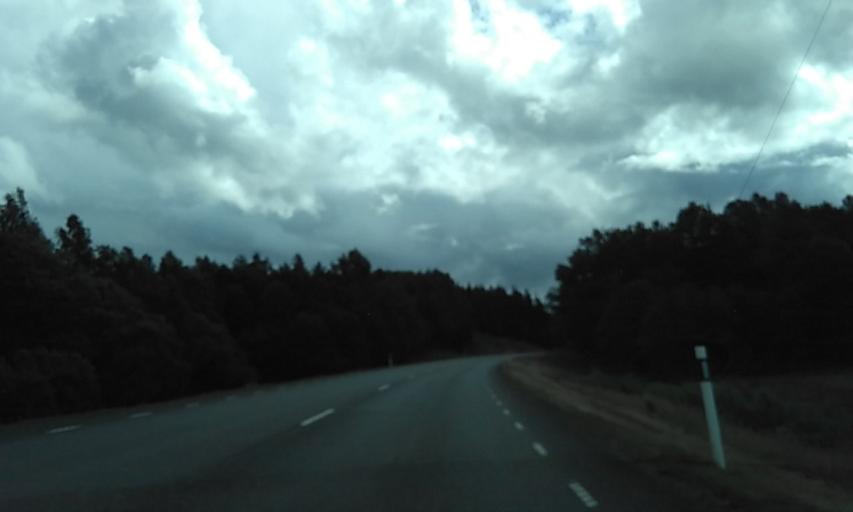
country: SE
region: Vaestra Goetaland
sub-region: Alingsas Kommun
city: Alingsas
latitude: 57.9726
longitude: 12.4425
